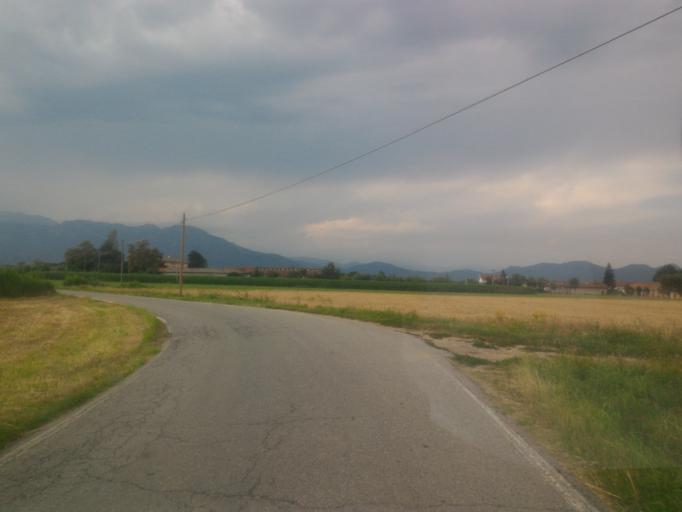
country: IT
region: Piedmont
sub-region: Provincia di Torino
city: Buriasco
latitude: 44.8845
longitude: 7.4018
